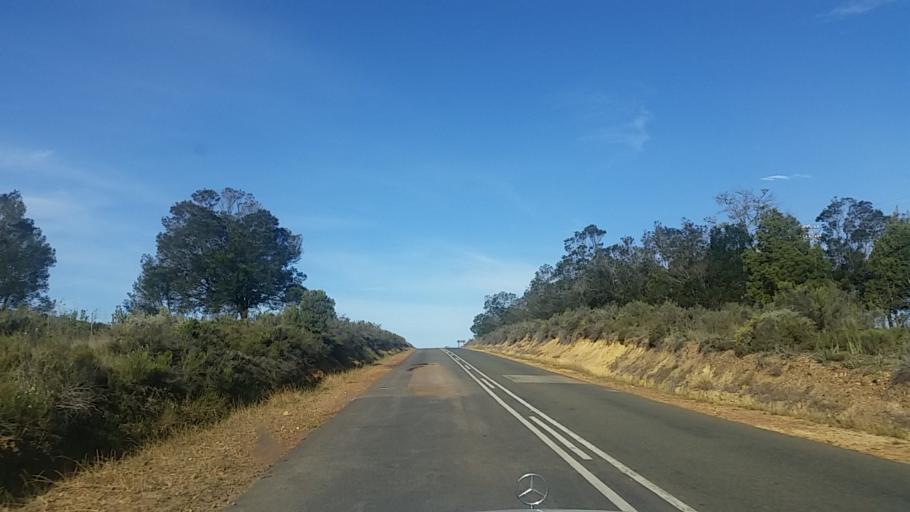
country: ZA
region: Western Cape
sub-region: Eden District Municipality
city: Knysna
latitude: -33.7634
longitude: 22.8364
